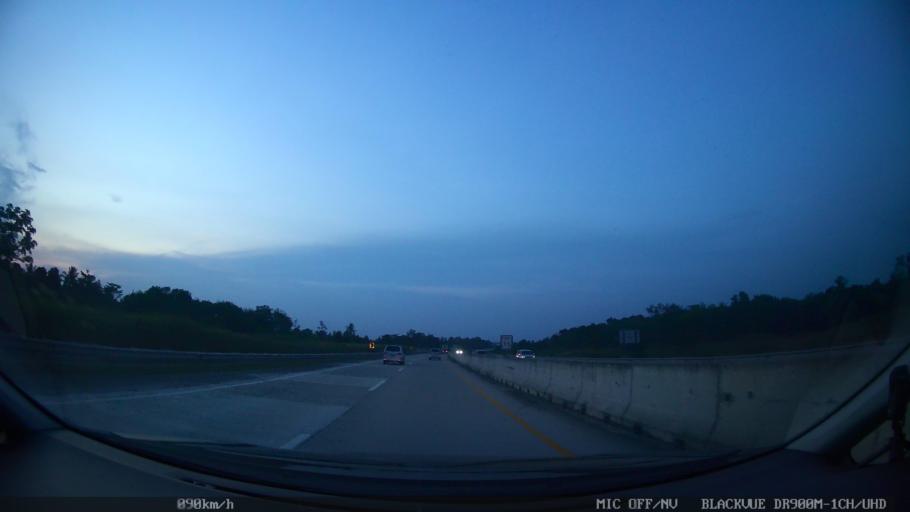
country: ID
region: Lampung
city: Sidorejo
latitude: -5.6403
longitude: 105.5722
